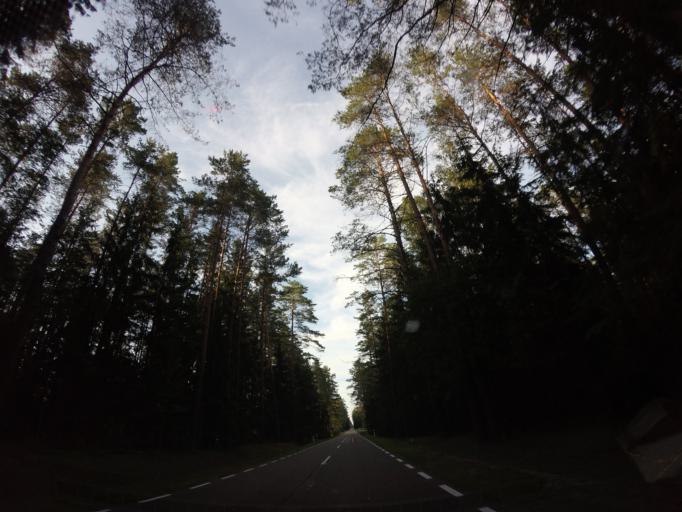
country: PL
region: Podlasie
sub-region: Powiat augustowski
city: Augustow
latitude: 53.9138
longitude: 23.1442
